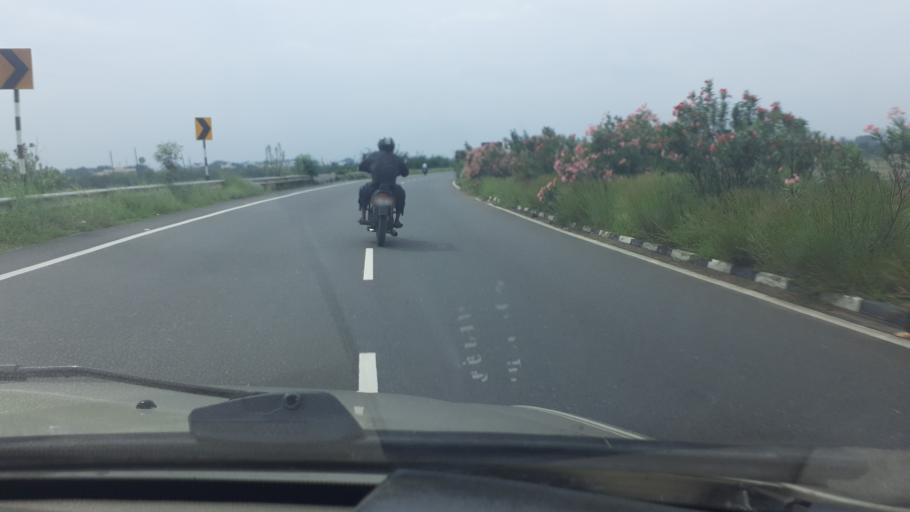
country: IN
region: Tamil Nadu
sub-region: Madurai
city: Tirupparangunram
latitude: 9.8352
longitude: 77.9998
